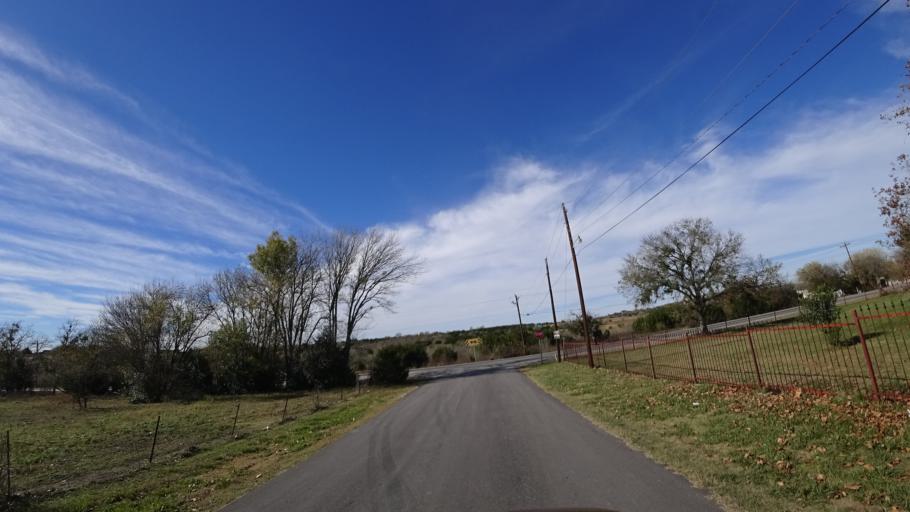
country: US
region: Texas
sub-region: Travis County
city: Onion Creek
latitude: 30.1069
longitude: -97.7234
